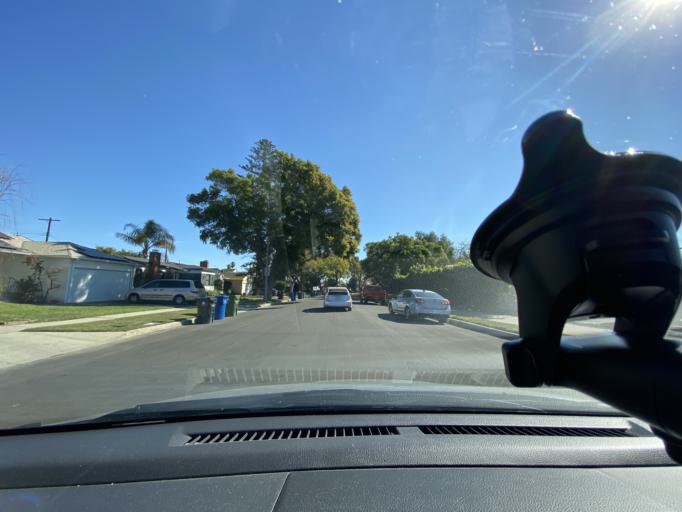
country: US
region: California
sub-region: Los Angeles County
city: Westwood, Los Angeles
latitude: 34.0283
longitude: -118.4382
